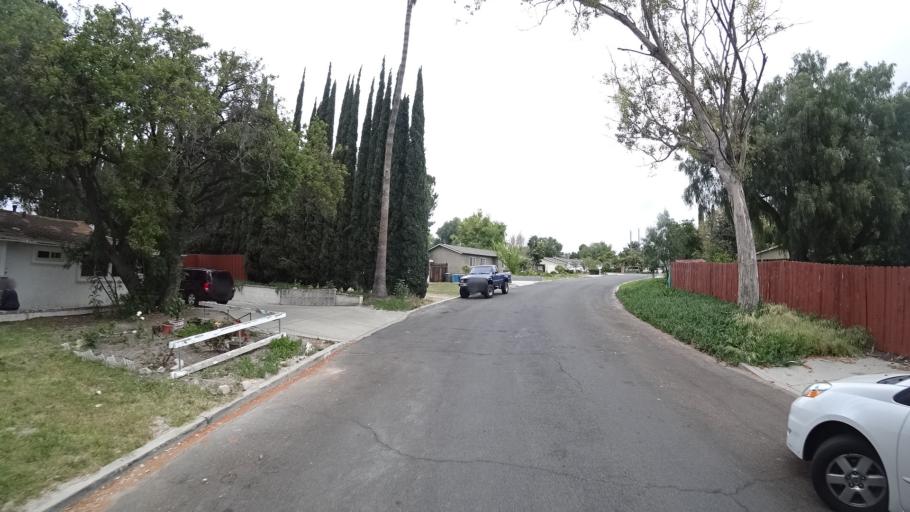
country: US
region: California
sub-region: Ventura County
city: Thousand Oaks
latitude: 34.2099
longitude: -118.8524
